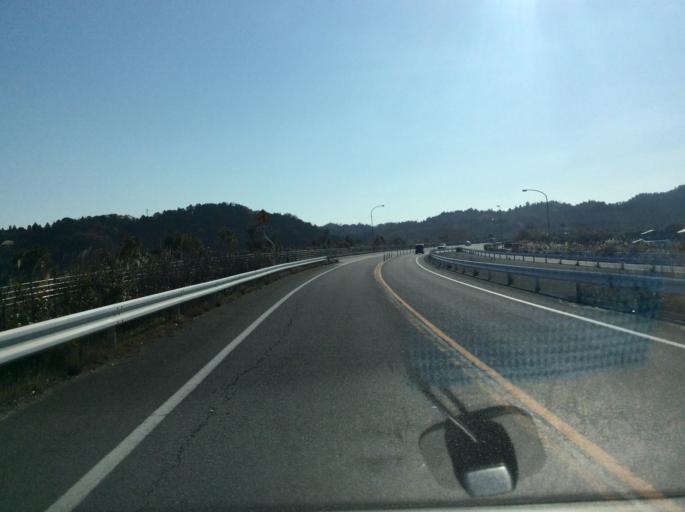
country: JP
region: Fukushima
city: Iwaki
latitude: 37.0543
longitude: 140.9437
